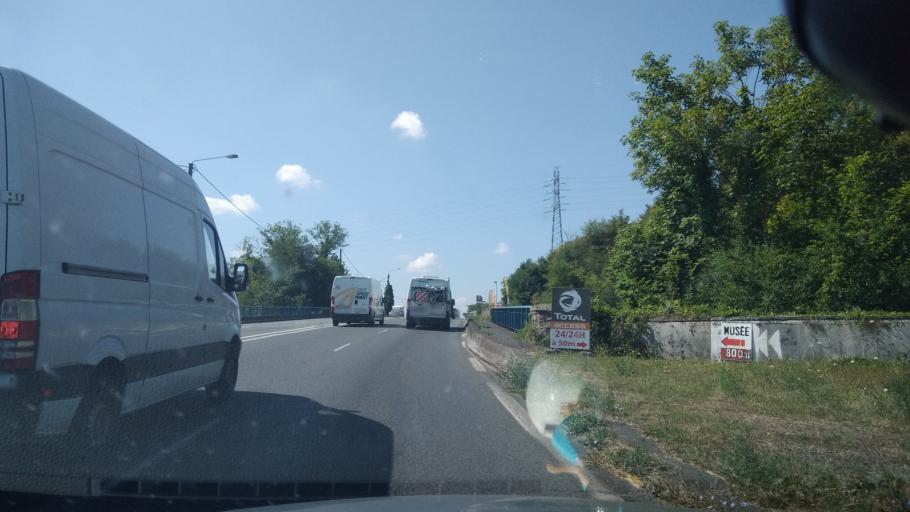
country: FR
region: Poitou-Charentes
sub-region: Departement de la Vienne
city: Chasseneuil-du-Poitou
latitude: 46.6334
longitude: 0.3575
